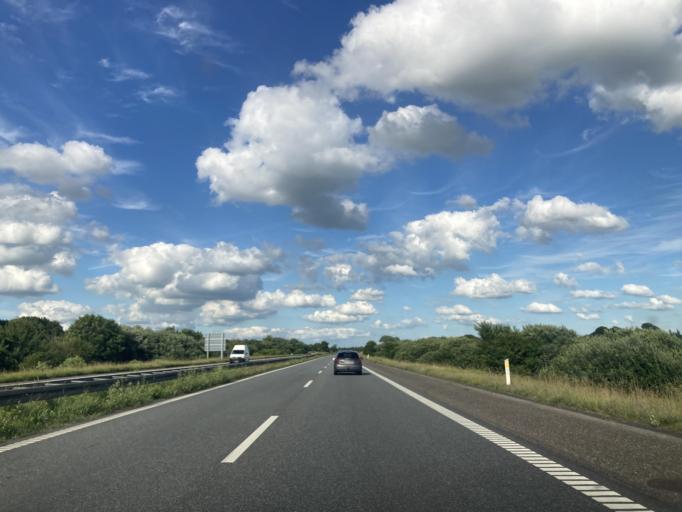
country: DK
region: South Denmark
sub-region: Vejen Kommune
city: Vejen
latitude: 55.4944
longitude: 9.1889
